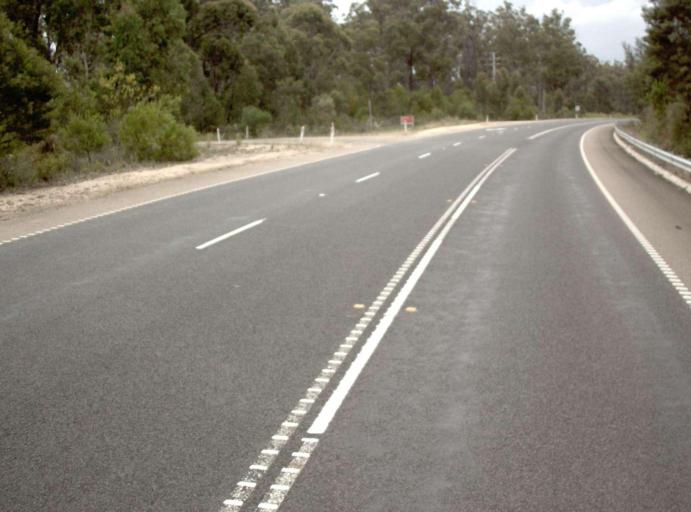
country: AU
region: Victoria
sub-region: East Gippsland
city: Lakes Entrance
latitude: -37.7196
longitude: 148.0792
